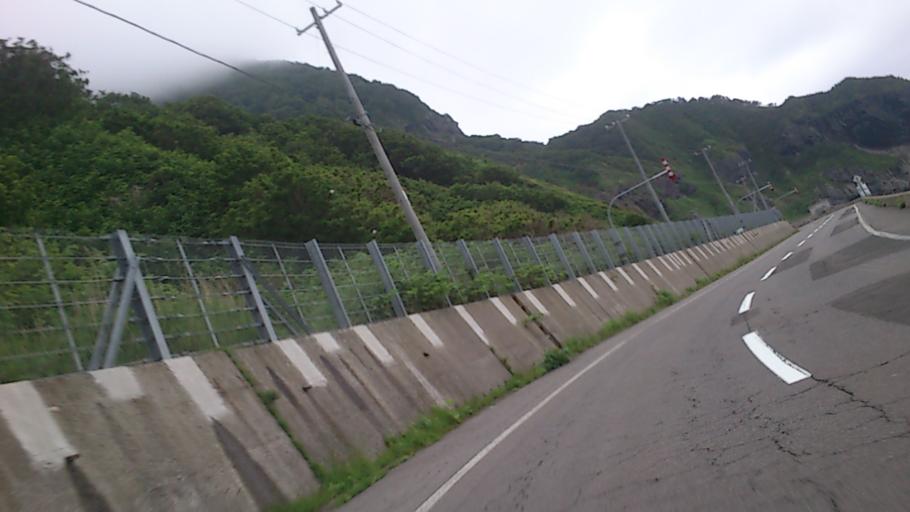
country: JP
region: Hokkaido
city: Iwanai
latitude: 42.6679
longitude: 139.8787
